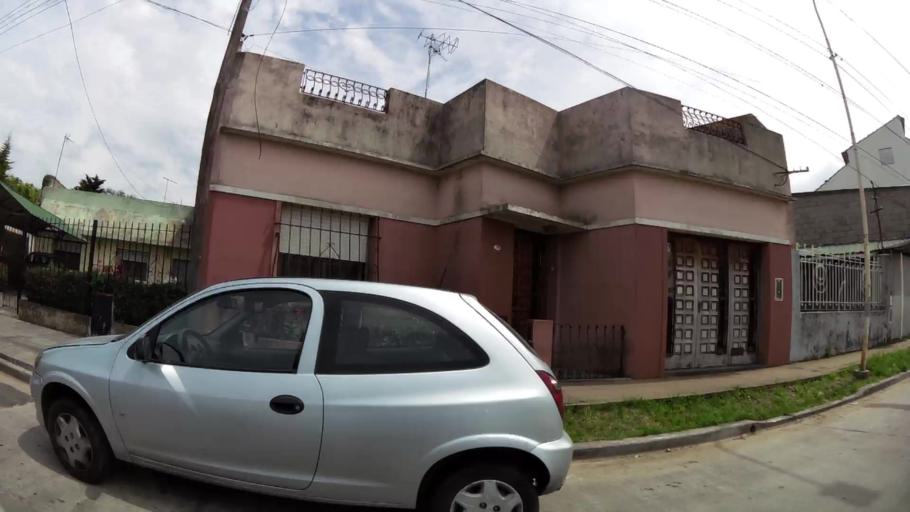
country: AR
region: Buenos Aires F.D.
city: Villa Lugano
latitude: -34.6850
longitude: -58.4957
